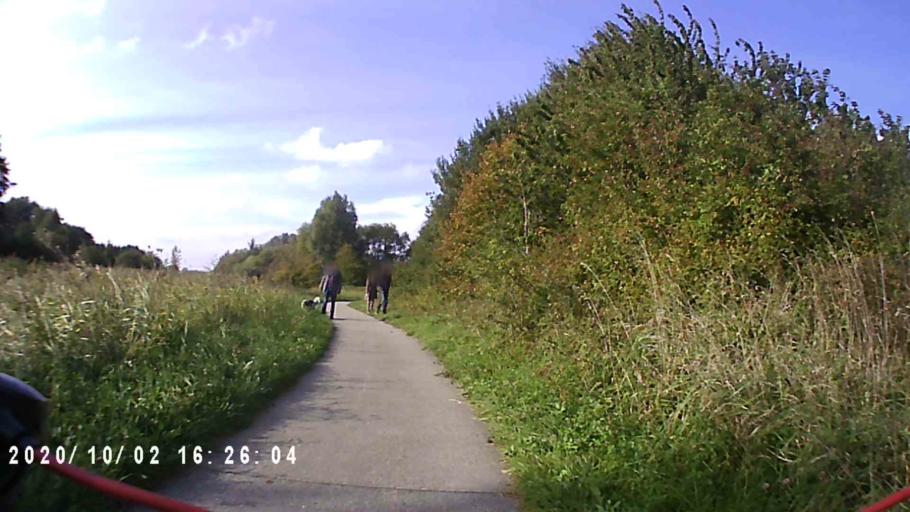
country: NL
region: Groningen
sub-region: Gemeente Zuidhorn
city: Grijpskerk
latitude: 53.2853
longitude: 6.3125
